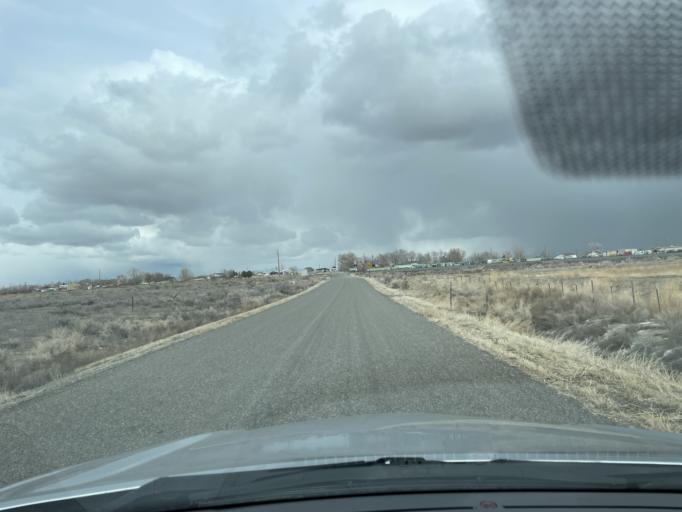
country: US
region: Colorado
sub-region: Mesa County
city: Loma
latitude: 39.1890
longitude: -108.8036
